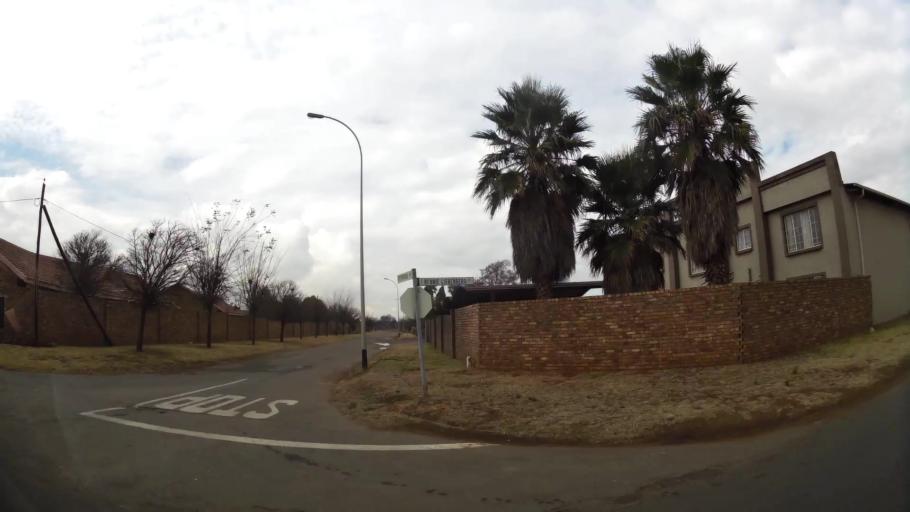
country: ZA
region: Gauteng
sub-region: Sedibeng District Municipality
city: Meyerton
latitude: -26.5770
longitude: 28.0068
